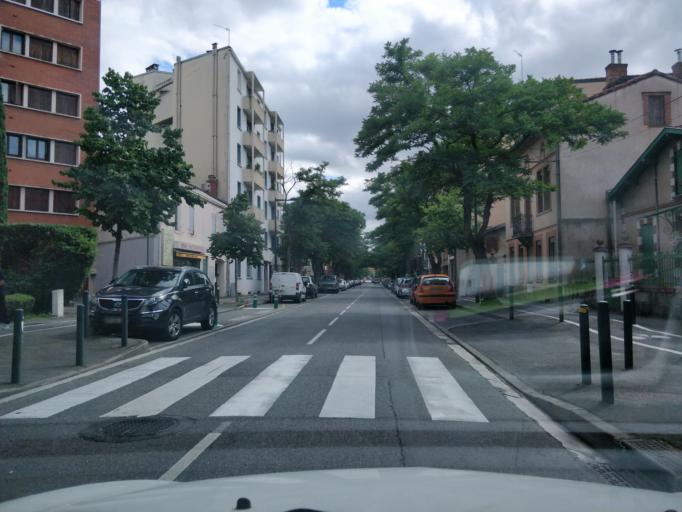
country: FR
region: Midi-Pyrenees
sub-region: Departement de la Haute-Garonne
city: Toulouse
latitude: 43.5936
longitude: 1.4207
